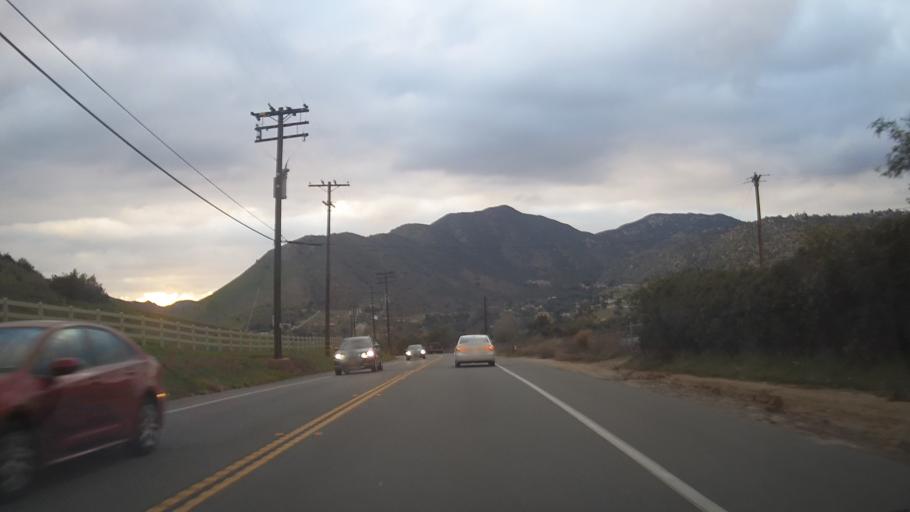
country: US
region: California
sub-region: San Diego County
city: Harbison Canyon
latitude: 32.7909
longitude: -116.8341
